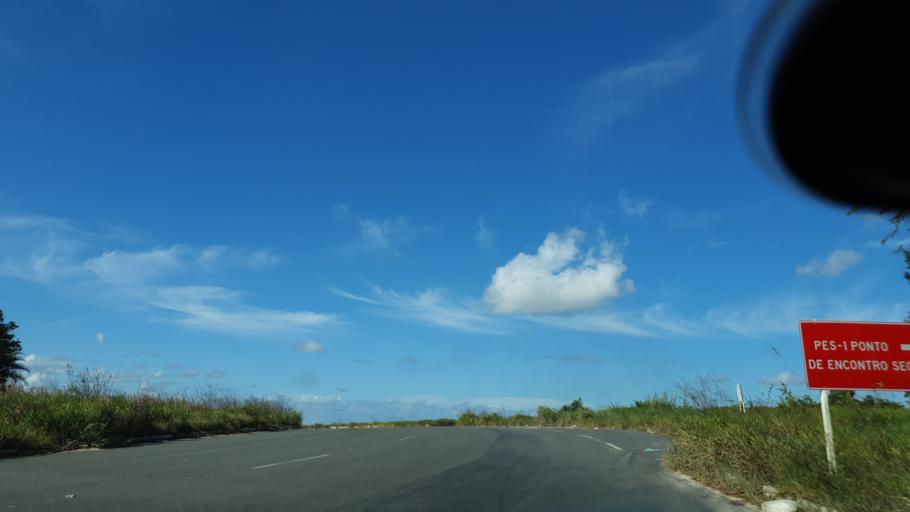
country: BR
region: Bahia
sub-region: Camacari
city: Camacari
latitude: -12.6805
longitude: -38.2816
